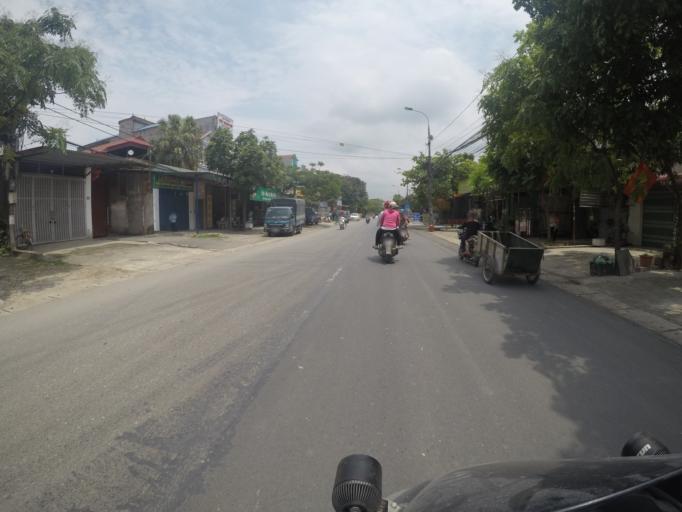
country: VN
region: Ha Noi
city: Soc Son
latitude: 21.2056
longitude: 105.8489
